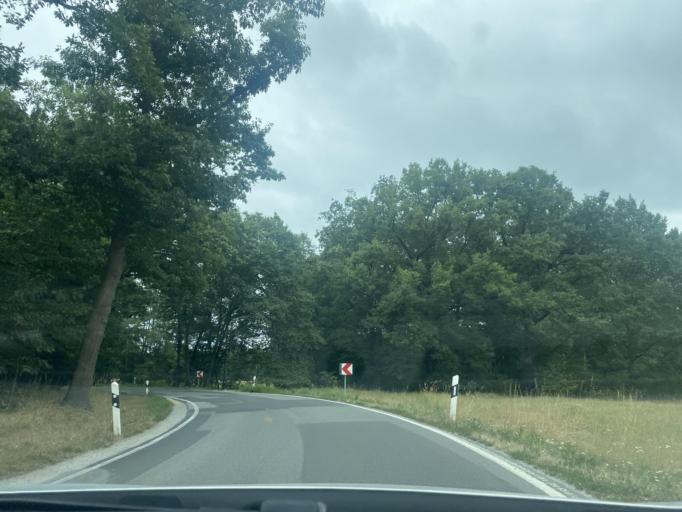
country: DE
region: Saxony
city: Grossdubrau
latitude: 51.2820
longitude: 14.4999
